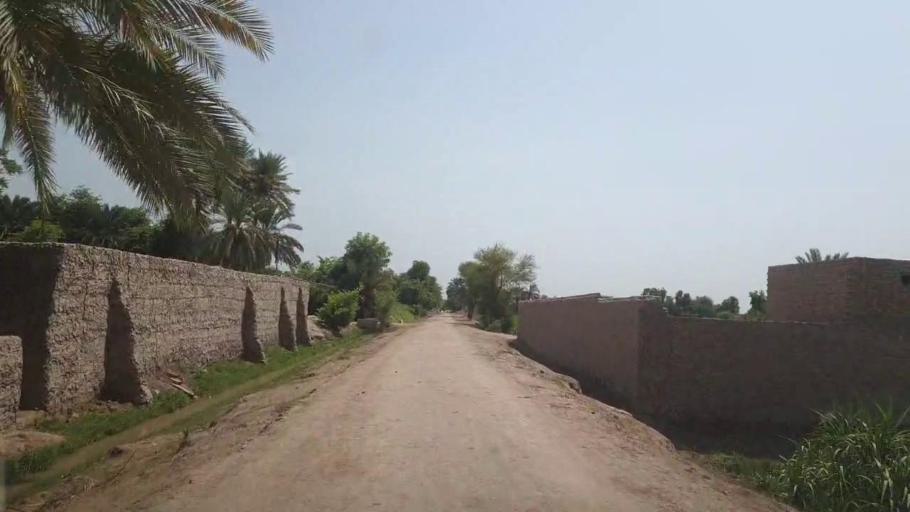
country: PK
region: Sindh
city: Sobhadero
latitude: 27.4398
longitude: 68.4022
